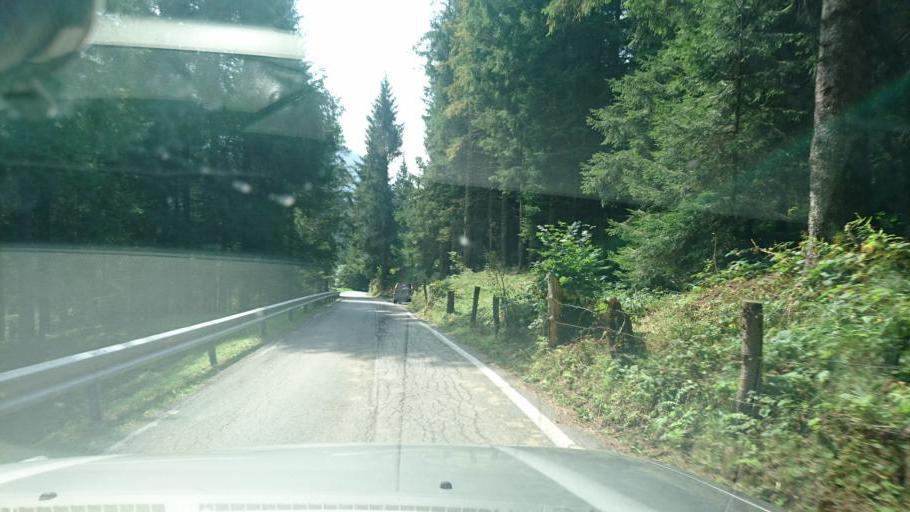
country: IT
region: Lombardy
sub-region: Provincia di Brescia
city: Bagolino
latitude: 45.9015
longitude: 10.4629
